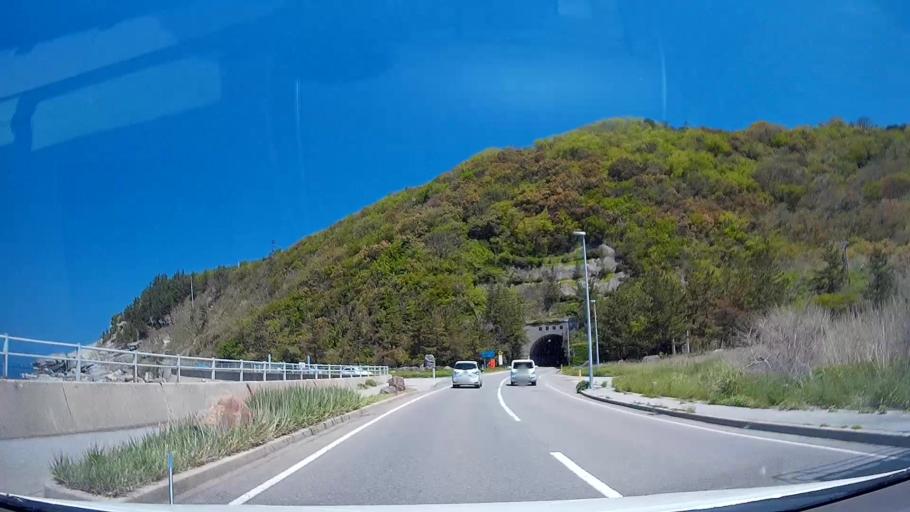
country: JP
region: Ishikawa
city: Nanao
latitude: 37.4738
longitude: 137.0931
